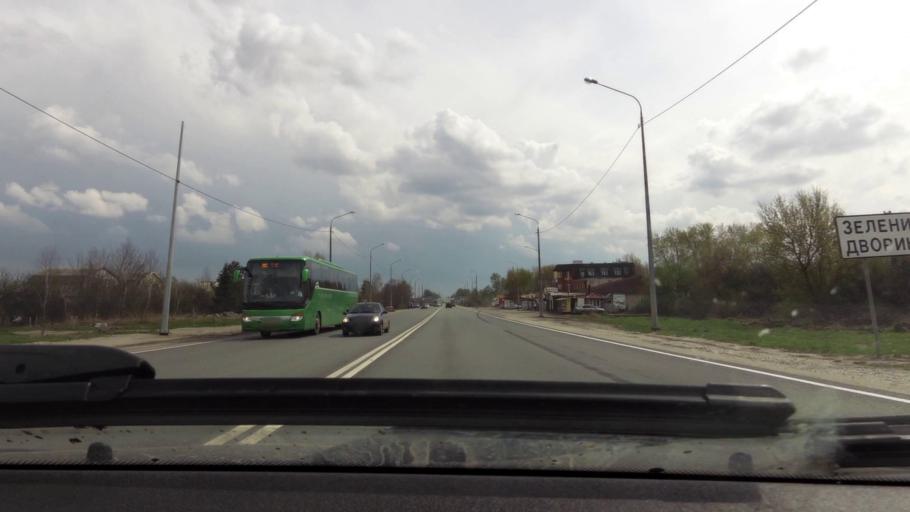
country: RU
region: Rjazan
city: Bagramovo
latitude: 54.7329
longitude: 39.4588
